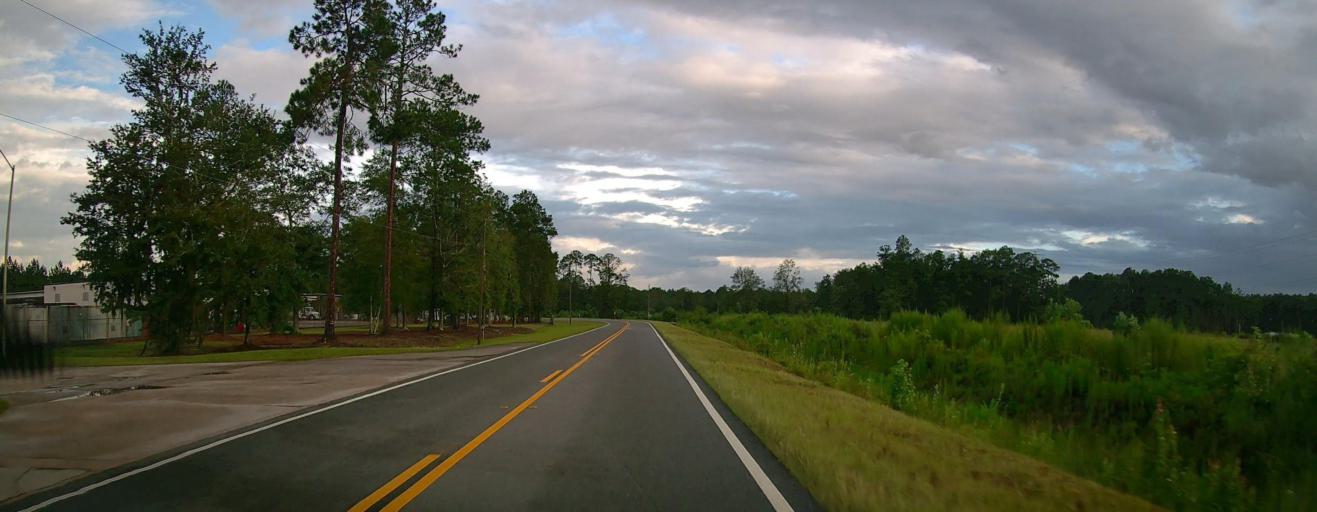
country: US
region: Georgia
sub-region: Ware County
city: Deenwood
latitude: 31.1969
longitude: -82.4015
